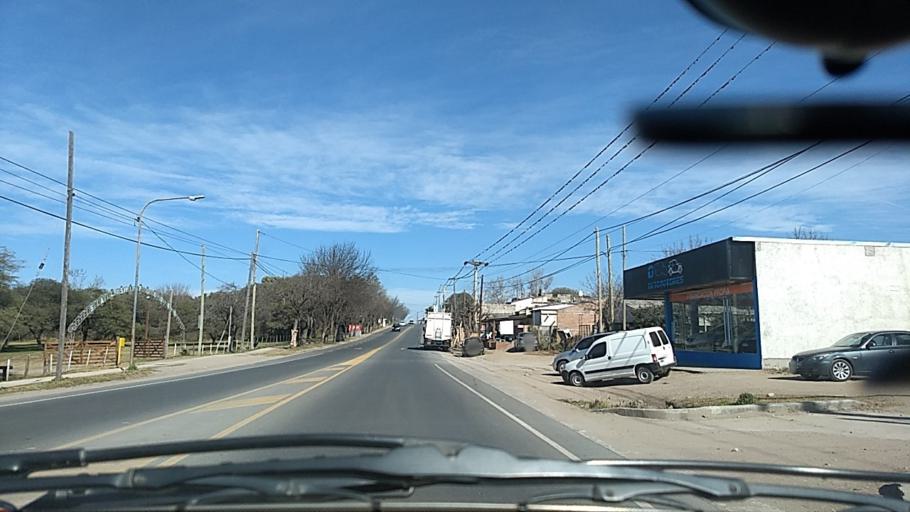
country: AR
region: Cordoba
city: Salsipuedes
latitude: -31.1289
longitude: -64.2949
